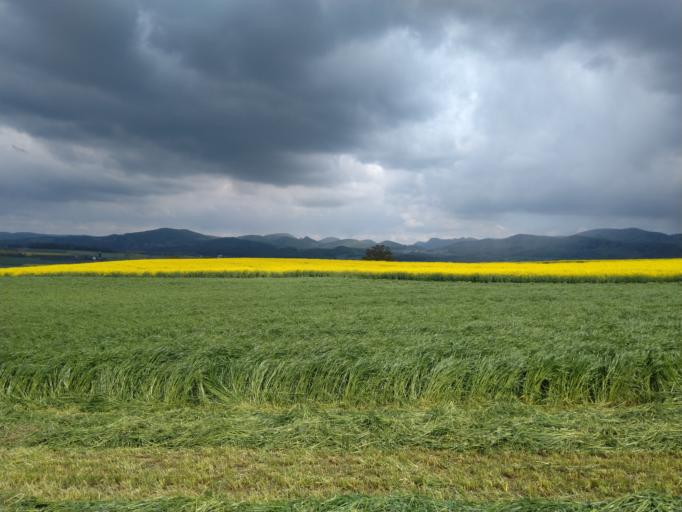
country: CH
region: Basel-Landschaft
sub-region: Bezirk Laufen
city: Laufen
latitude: 47.4054
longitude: 7.4979
